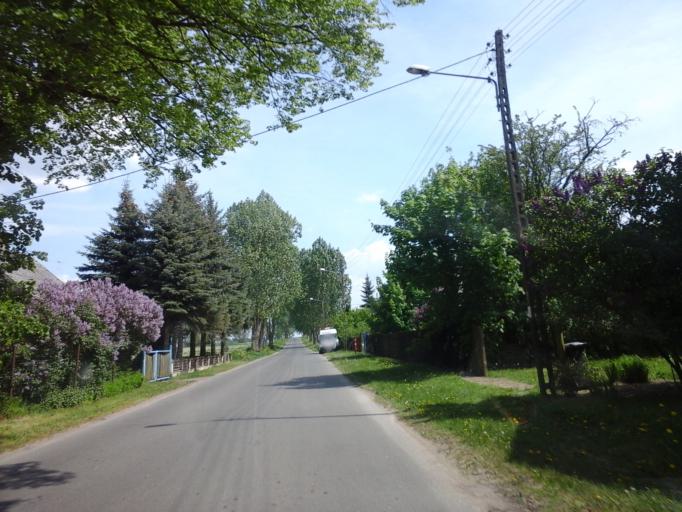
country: PL
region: West Pomeranian Voivodeship
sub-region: Powiat choszczenski
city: Choszczno
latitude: 53.1306
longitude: 15.4468
